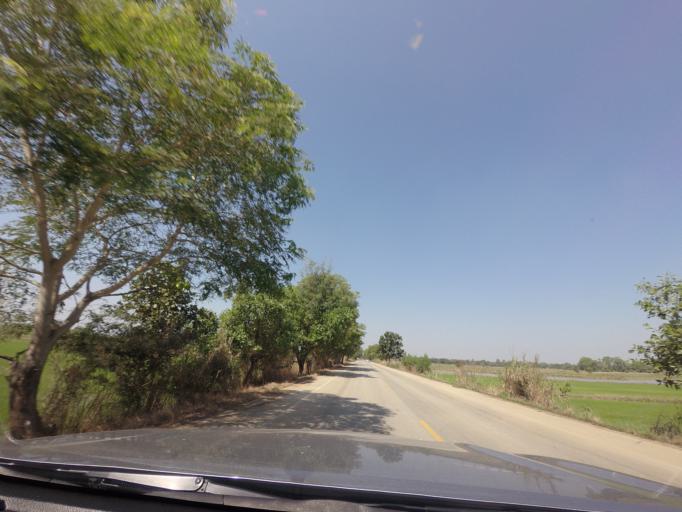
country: TH
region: Sukhothai
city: Ban Na
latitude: 17.1031
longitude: 99.7820
